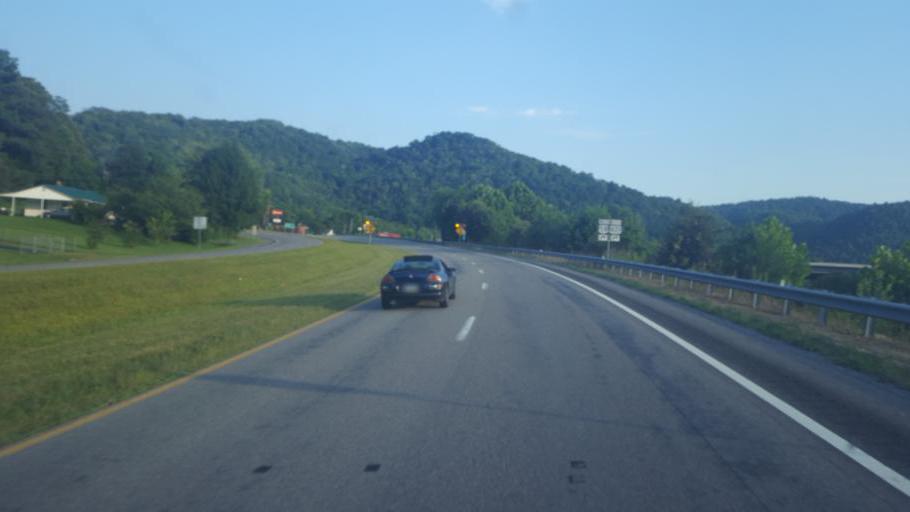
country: US
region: Virginia
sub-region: Lee County
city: Dryden
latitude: 36.7143
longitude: -82.7956
